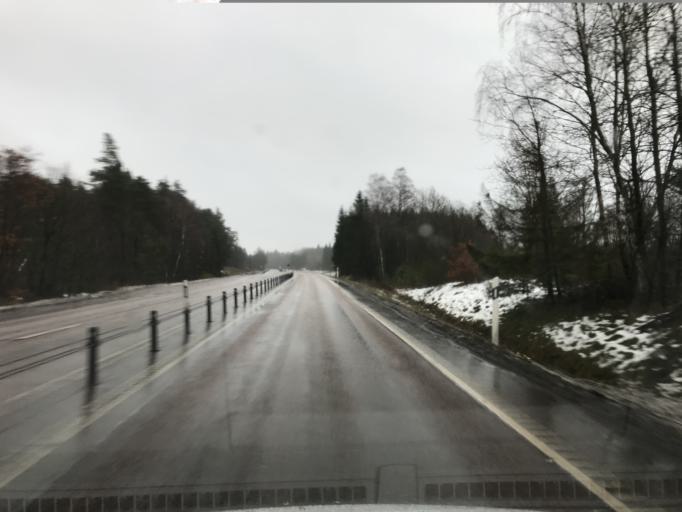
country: SE
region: Skane
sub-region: Perstorps Kommun
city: Perstorp
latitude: 56.1387
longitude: 13.4842
